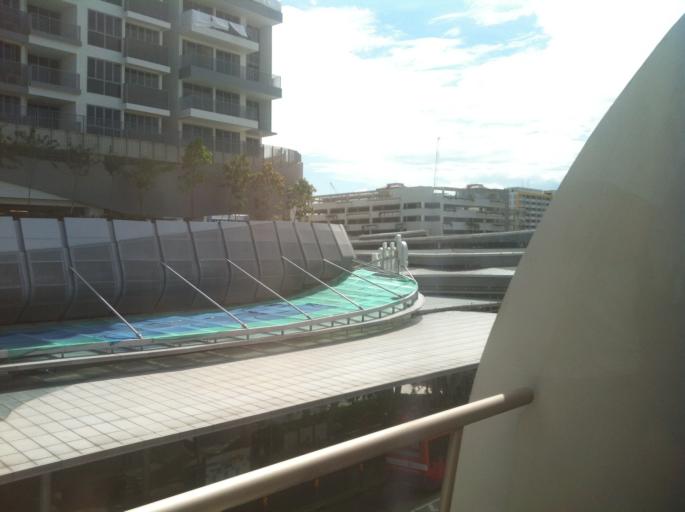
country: SG
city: Singapore
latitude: 1.3241
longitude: 103.9297
